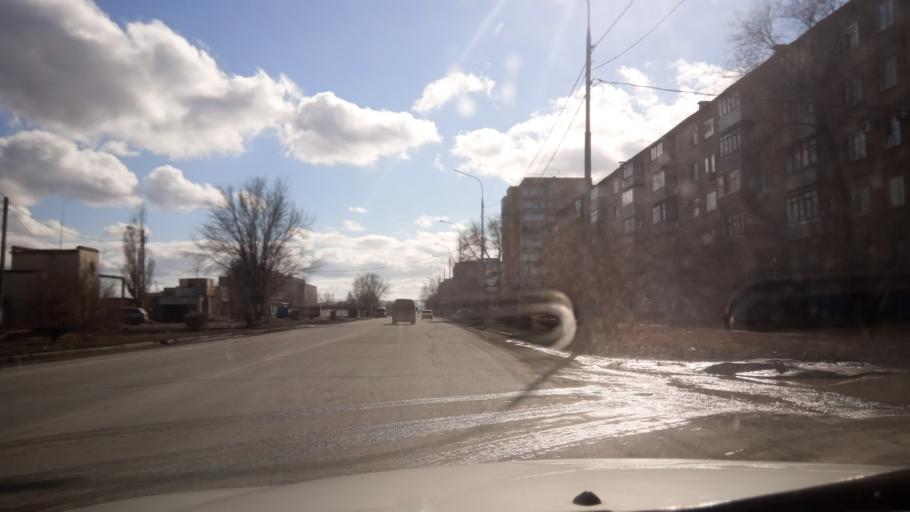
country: RU
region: Orenburg
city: Novotroitsk
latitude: 51.1861
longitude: 58.2867
